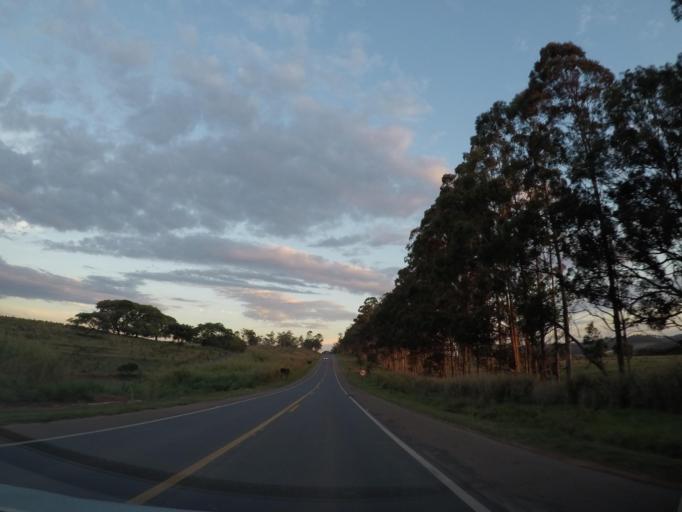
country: BR
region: Sao Paulo
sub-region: Itupeva
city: Itupeva
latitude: -23.0463
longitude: -47.0960
